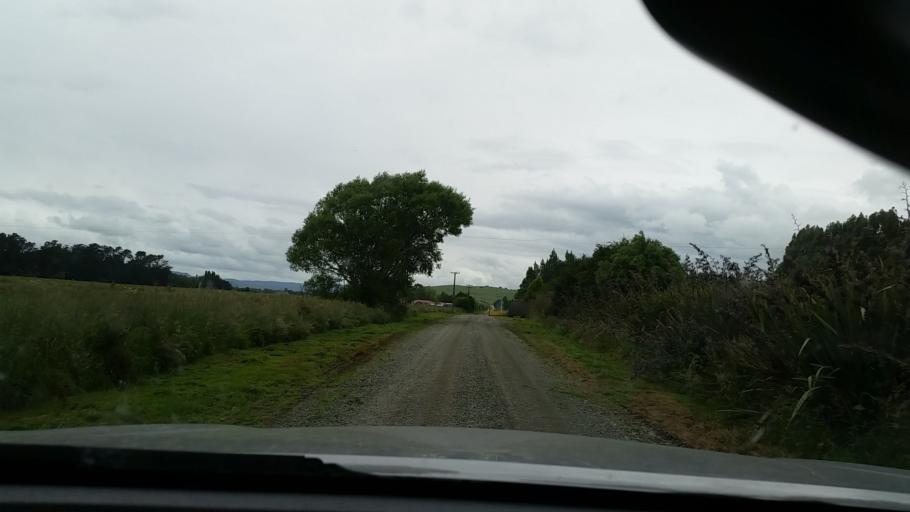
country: NZ
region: Southland
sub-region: Southland District
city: Winton
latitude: -46.0996
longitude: 168.3186
